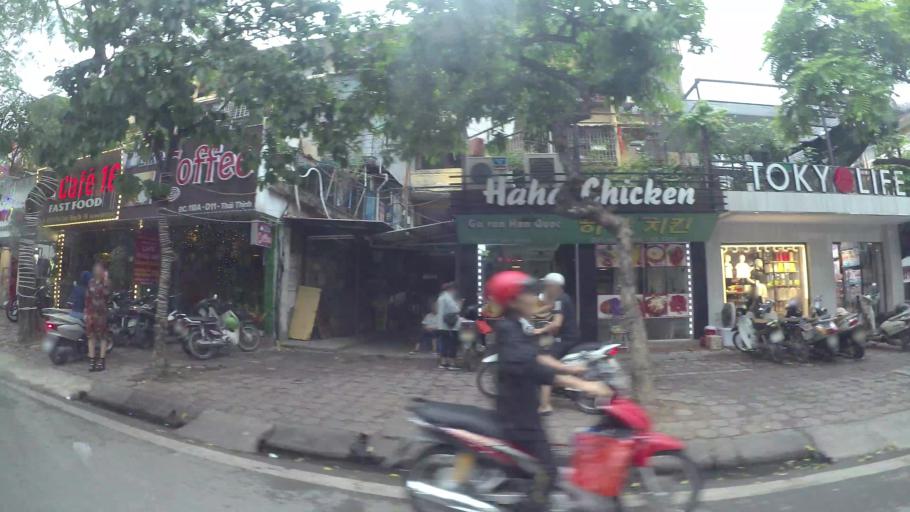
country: VN
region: Ha Noi
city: Dong Da
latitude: 21.0097
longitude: 105.8190
